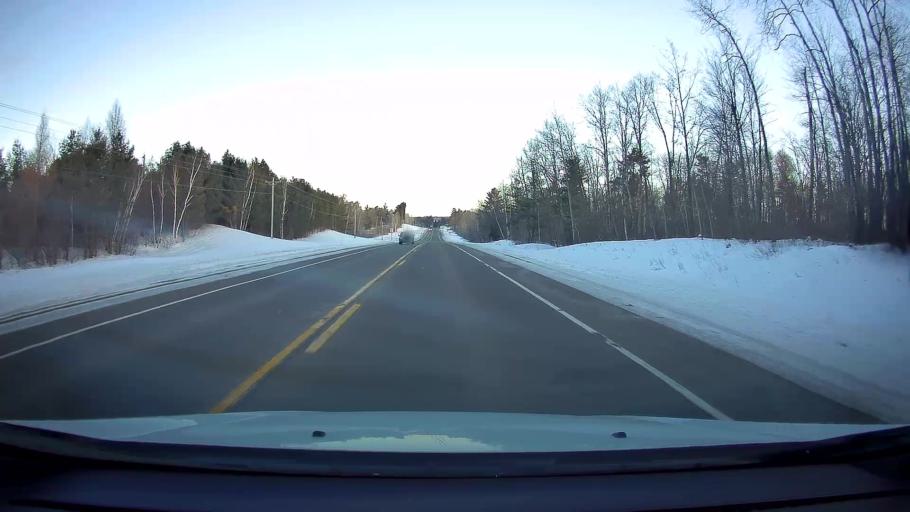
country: US
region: Wisconsin
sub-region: Barron County
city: Cumberland
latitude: 45.5907
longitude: -92.0177
